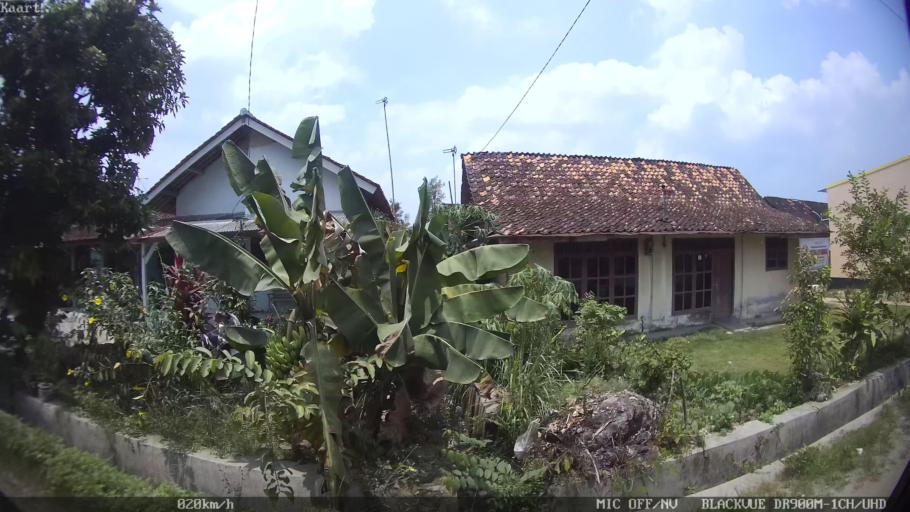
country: ID
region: Lampung
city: Pringsewu
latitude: -5.3484
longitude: 104.9870
